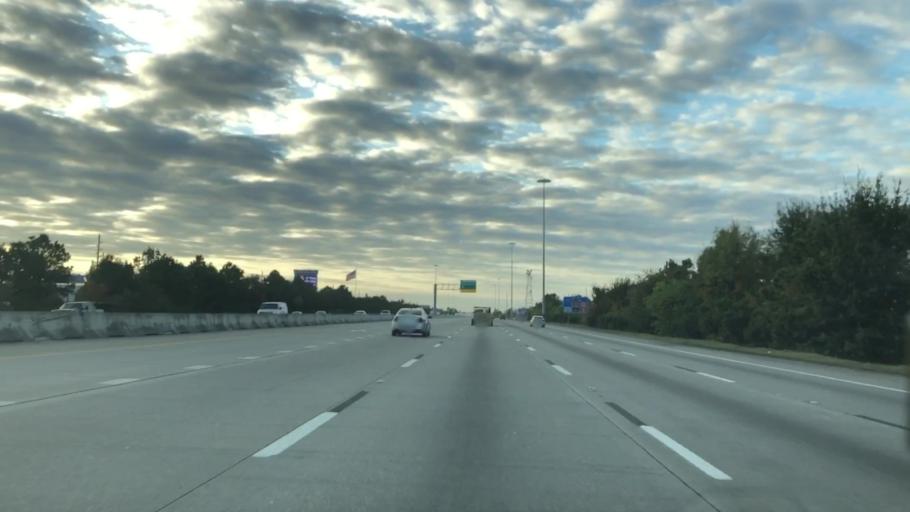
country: US
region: Texas
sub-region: Harris County
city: Spring
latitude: 30.0653
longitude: -95.4344
